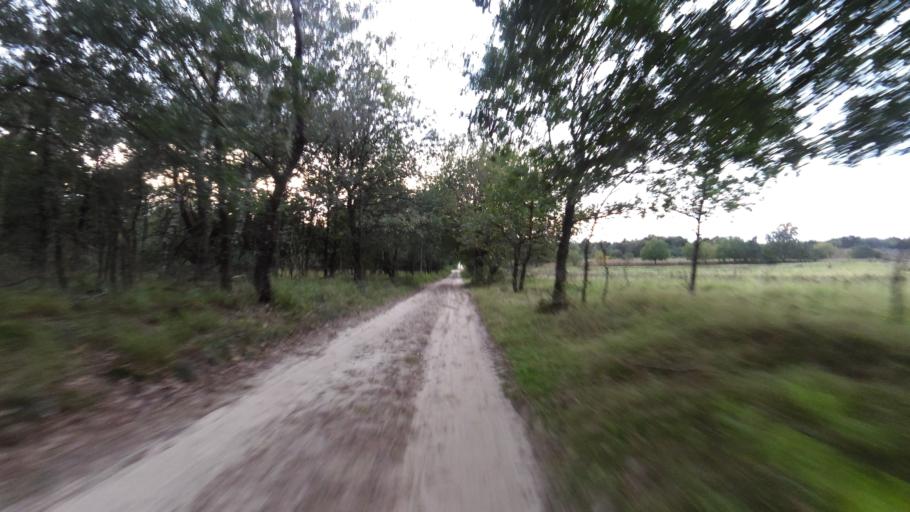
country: NL
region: Gelderland
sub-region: Gemeente Apeldoorn
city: Uddel
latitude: 52.1831
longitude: 5.8290
